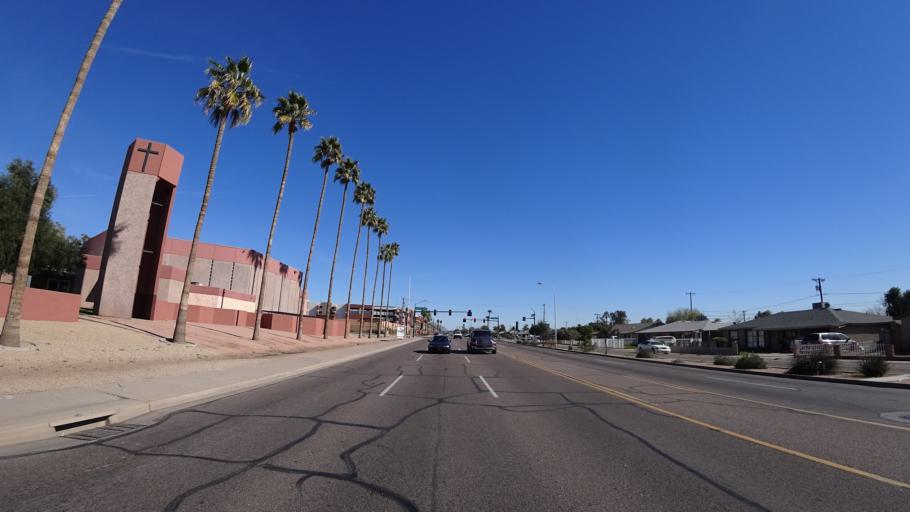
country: US
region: Arizona
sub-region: Maricopa County
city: Glendale
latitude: 33.5096
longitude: -112.1266
